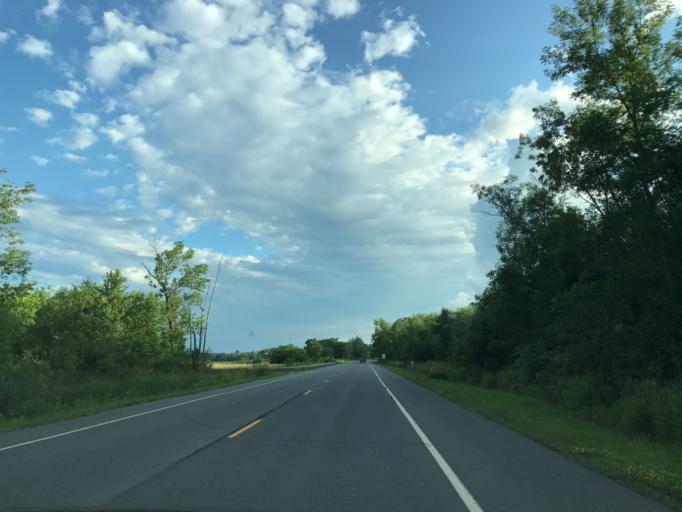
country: US
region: New York
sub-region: Saratoga County
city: Stillwater
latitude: 43.0070
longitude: -73.6030
